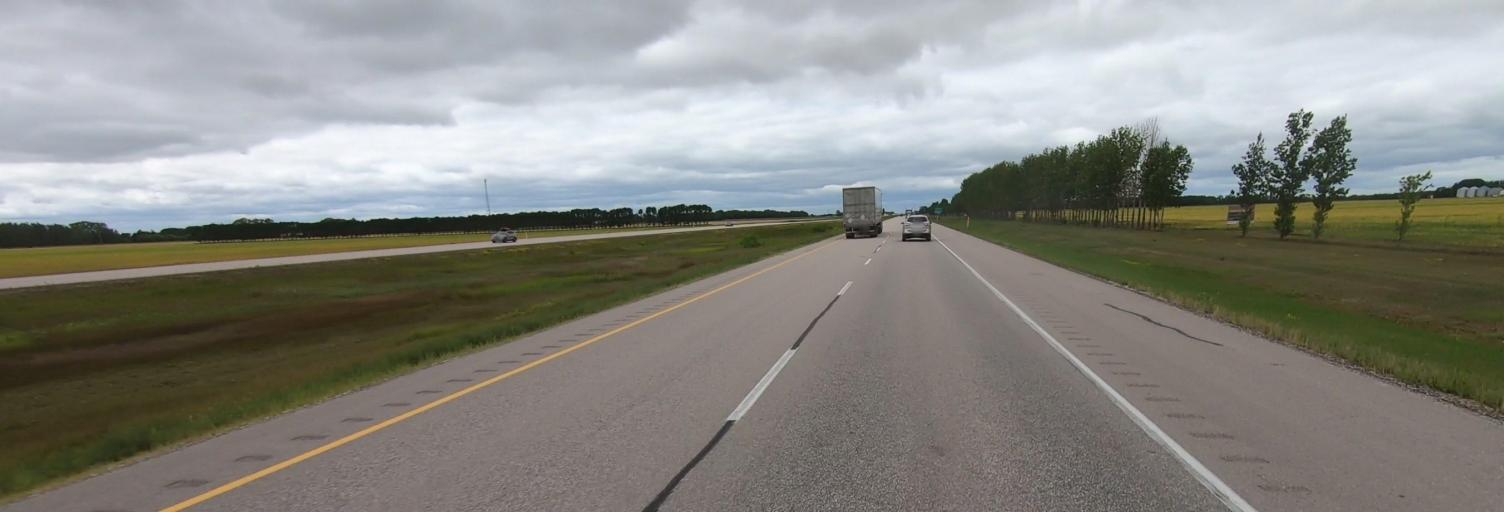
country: CA
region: Manitoba
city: Portage la Prairie
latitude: 49.9499
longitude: -97.9915
